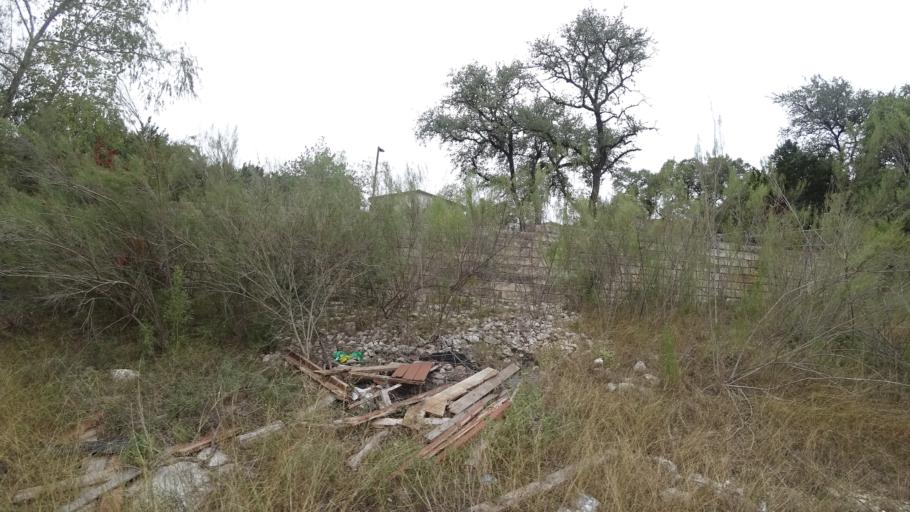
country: US
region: Texas
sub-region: Travis County
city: Lakeway
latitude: 30.3783
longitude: -97.9436
